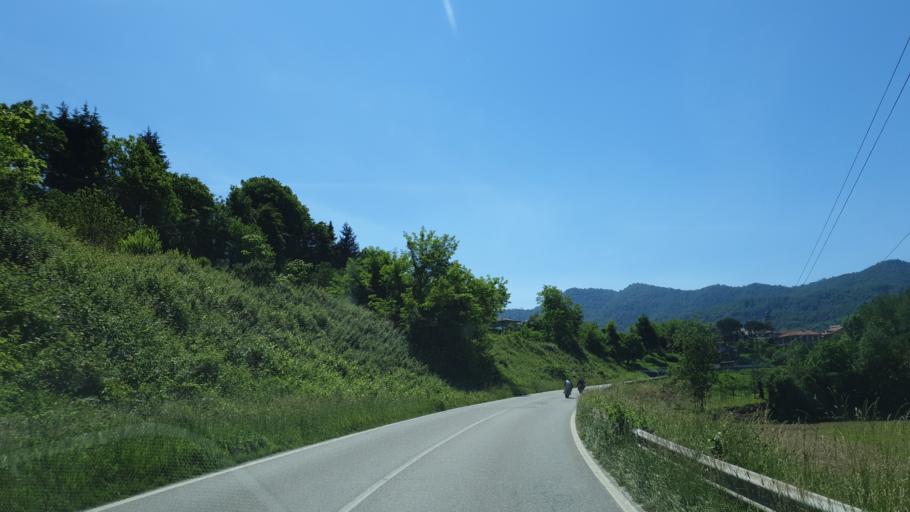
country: IT
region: Lombardy
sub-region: Provincia di Bergamo
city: Cisano Bergamasco
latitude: 45.7483
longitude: 9.4693
